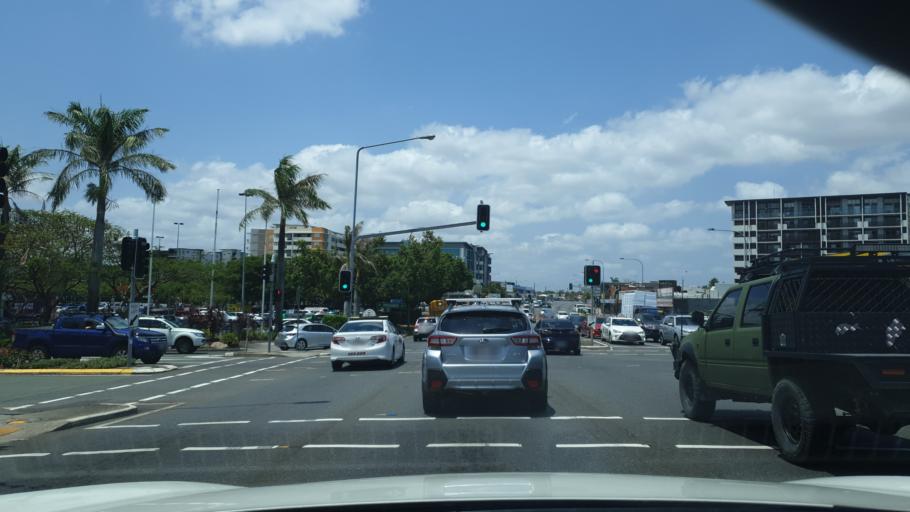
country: AU
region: Queensland
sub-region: Brisbane
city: Chermside West
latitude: -27.3843
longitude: 153.0304
